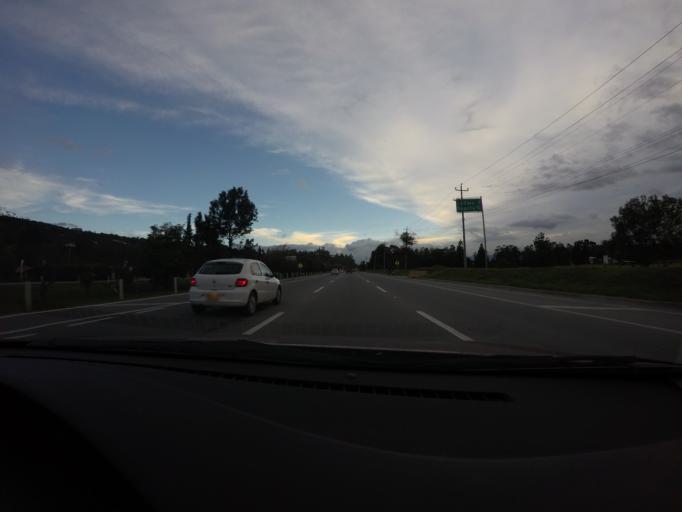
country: CO
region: Cundinamarca
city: Cajica
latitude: 4.8833
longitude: -74.0156
